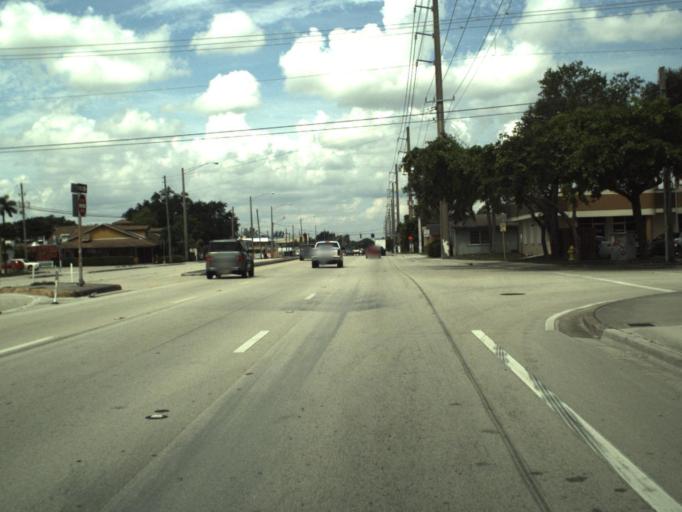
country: US
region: Florida
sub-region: Broward County
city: Dania Beach
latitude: 26.0626
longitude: -80.1762
